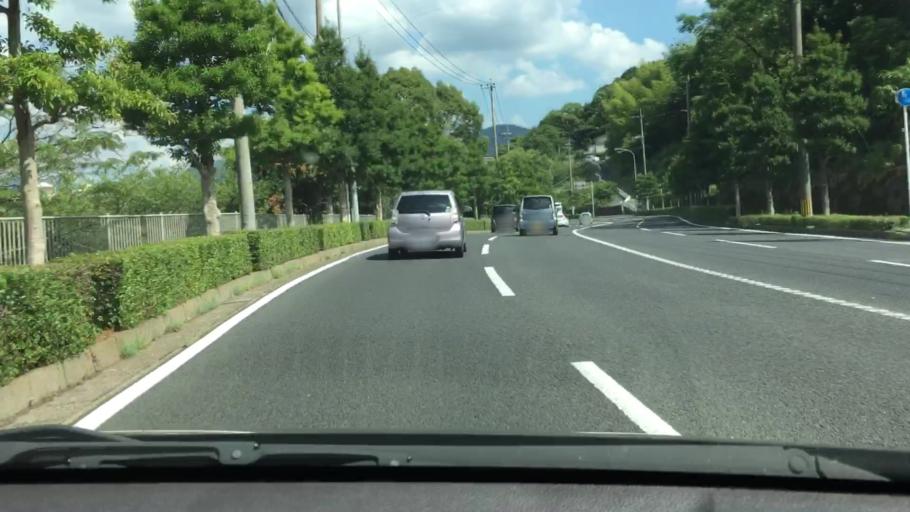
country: JP
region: Nagasaki
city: Sasebo
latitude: 33.2093
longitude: 129.7135
